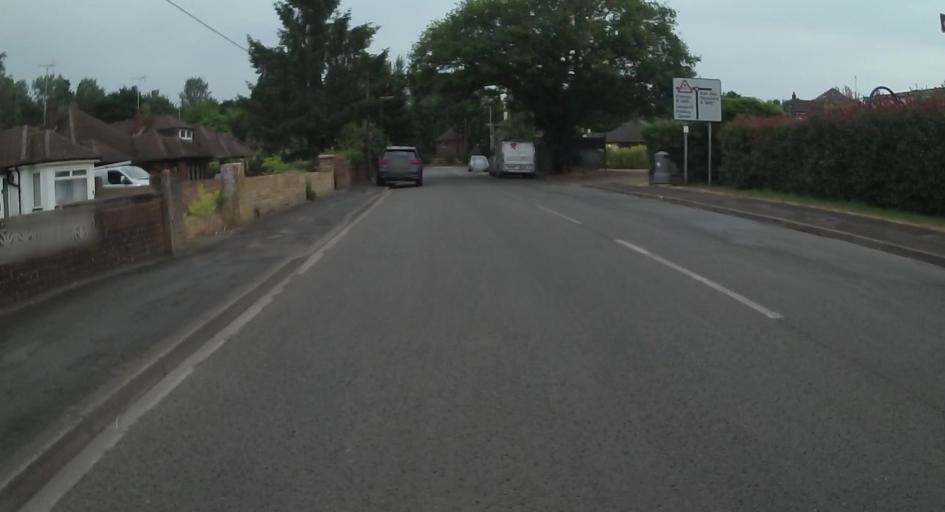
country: GB
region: England
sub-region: Surrey
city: Frimley
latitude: 51.2954
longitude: -0.7284
